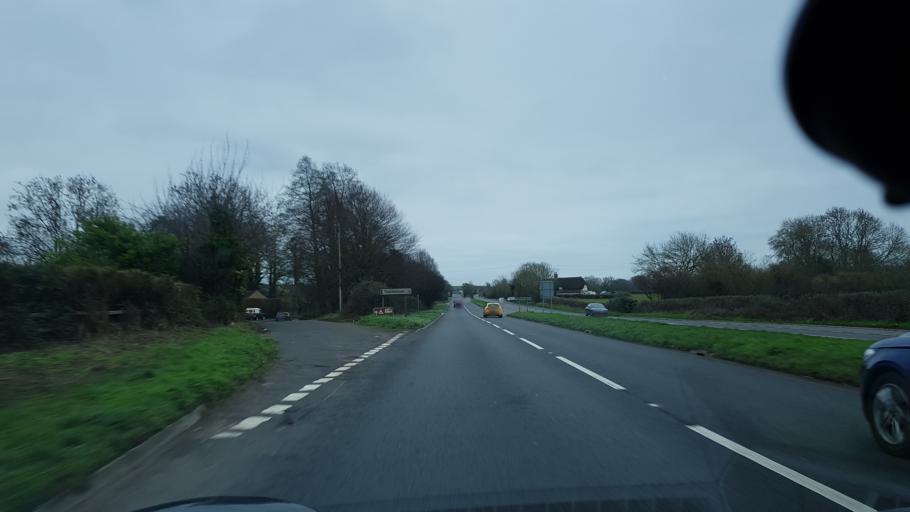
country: GB
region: England
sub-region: Somerset
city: Creech Saint Michael
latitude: 51.0089
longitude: -3.0348
